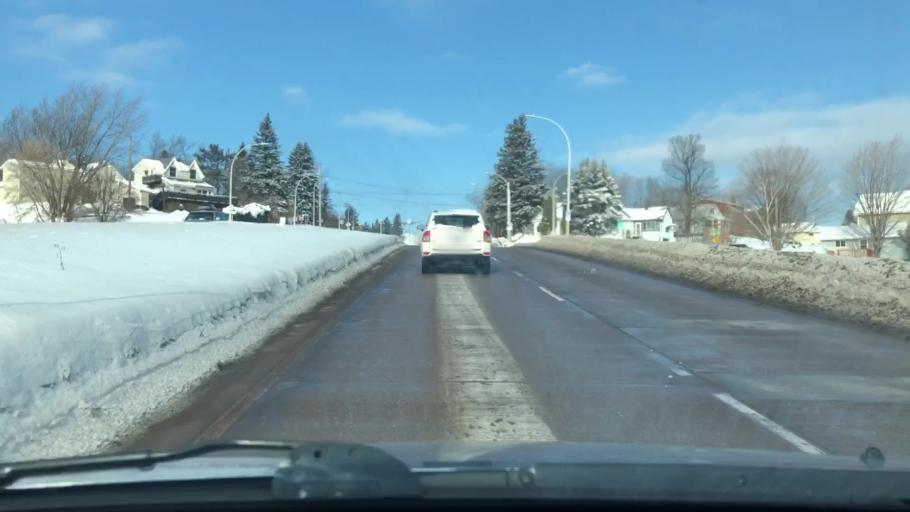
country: US
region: Minnesota
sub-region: Saint Louis County
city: Duluth
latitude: 46.7933
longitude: -92.1070
